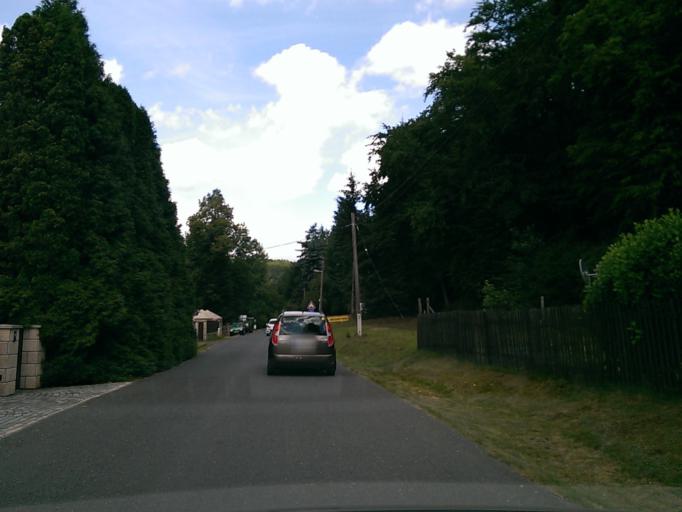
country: CZ
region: Central Bohemia
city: Mseno
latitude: 50.4281
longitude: 14.5801
